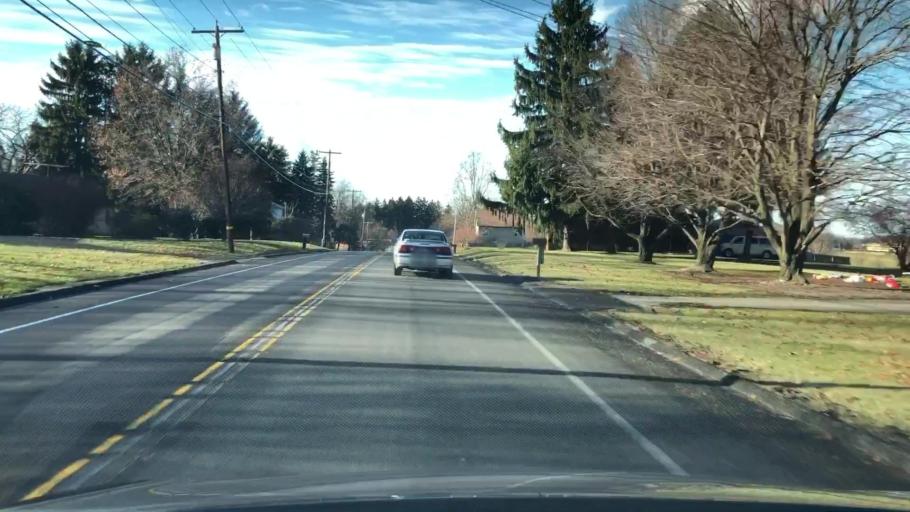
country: US
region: Pennsylvania
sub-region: Butler County
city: Saxonburg
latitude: 40.7703
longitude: -79.7906
